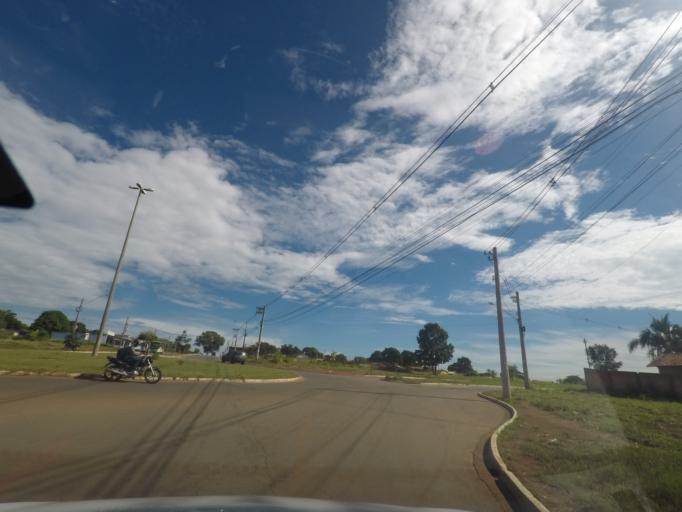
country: BR
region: Goias
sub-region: Aparecida De Goiania
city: Aparecida de Goiania
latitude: -16.8113
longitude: -49.2807
